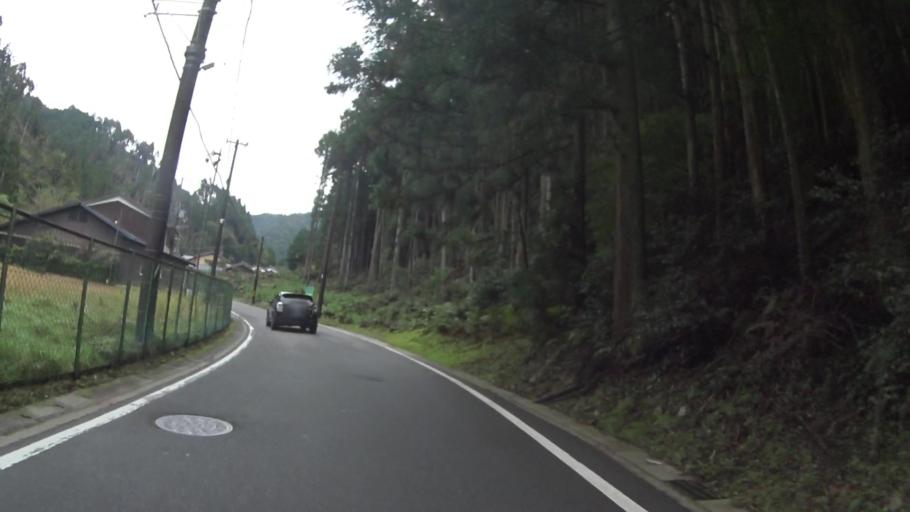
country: JP
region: Kyoto
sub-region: Kyoto-shi
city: Kamigyo-ku
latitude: 35.1093
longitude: 135.7673
